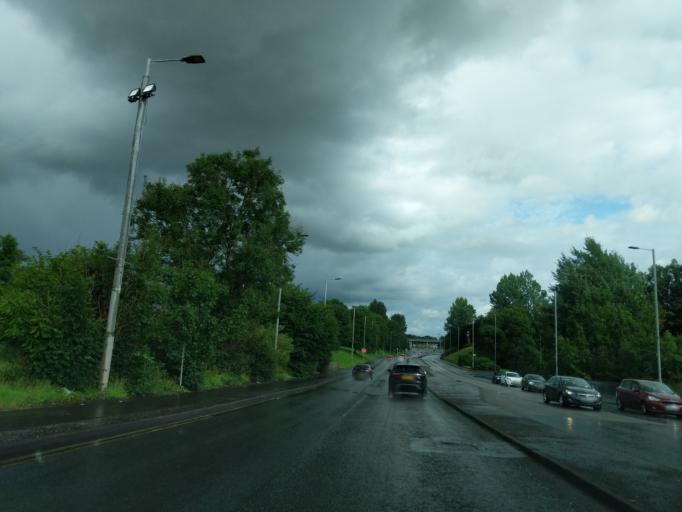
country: GB
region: Scotland
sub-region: East Renfrewshire
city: Newton Mearns
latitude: 55.8076
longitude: -4.3476
